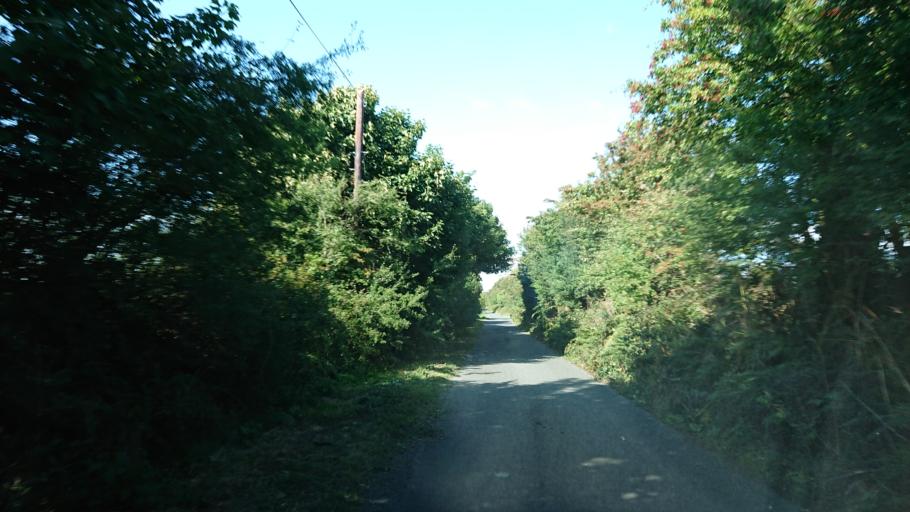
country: IE
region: Munster
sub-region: Waterford
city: Waterford
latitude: 52.2210
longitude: -7.0566
